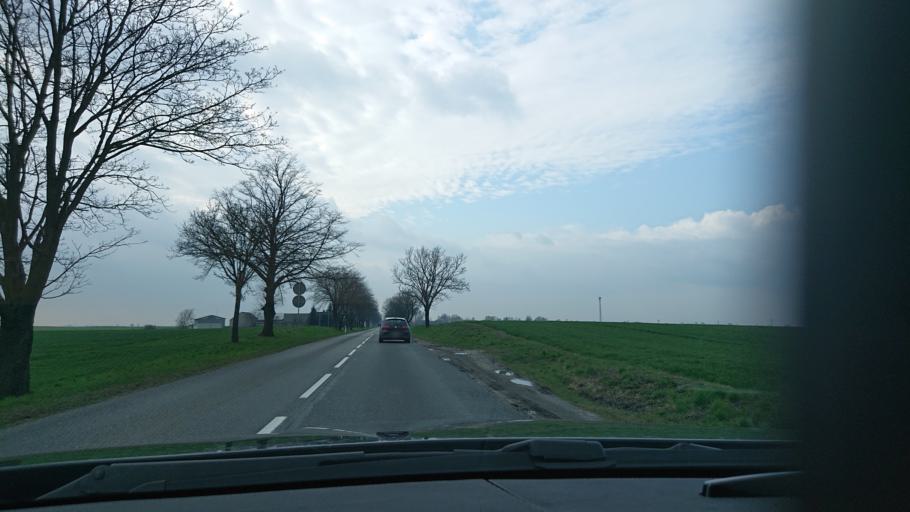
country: PL
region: Greater Poland Voivodeship
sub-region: Powiat gnieznienski
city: Gniezno
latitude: 52.5565
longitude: 17.5371
